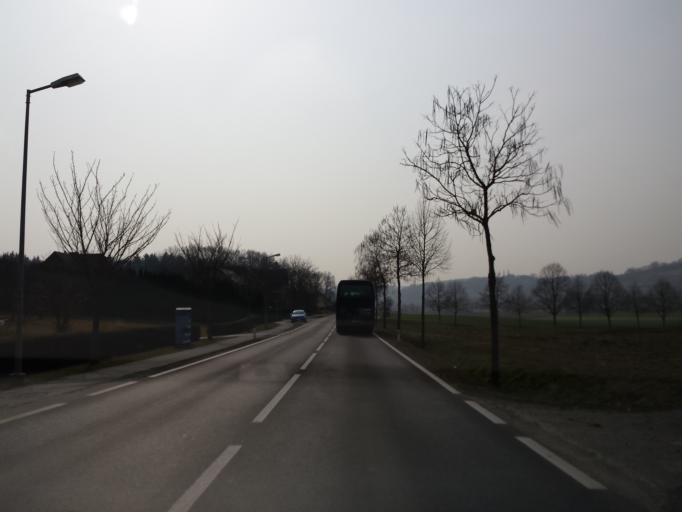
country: AT
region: Styria
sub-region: Politischer Bezirk Hartberg-Fuerstenfeld
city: Fuerstenfeld
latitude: 47.0271
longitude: 16.0919
